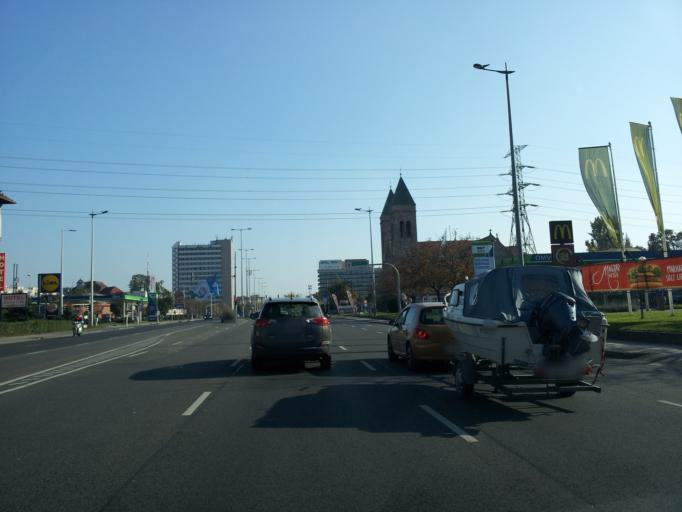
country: HU
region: Budapest
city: Budapest XX. keruelet
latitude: 47.4724
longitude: 19.1072
